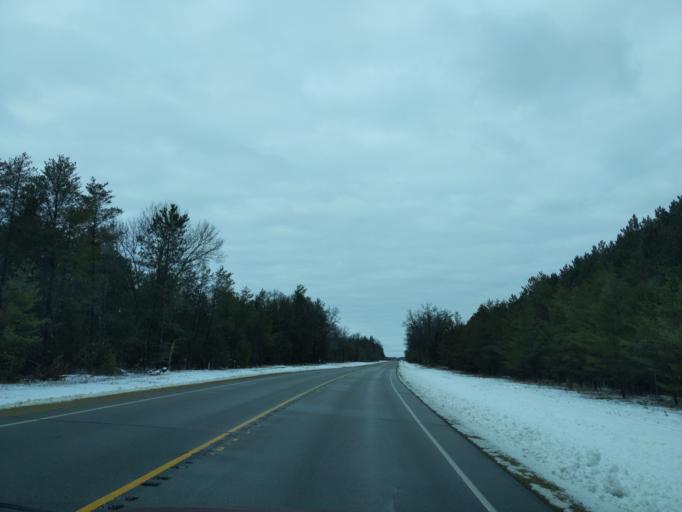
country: US
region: Wisconsin
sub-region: Waushara County
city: Wautoma
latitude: 43.9686
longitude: -89.3275
